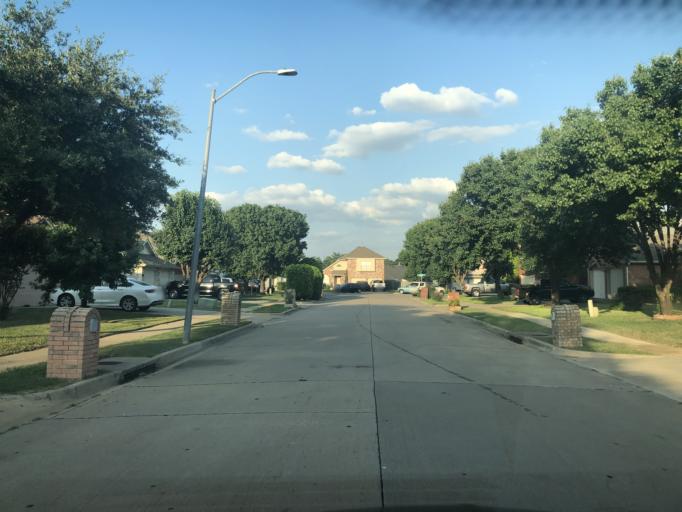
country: US
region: Texas
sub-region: Dallas County
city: Irving
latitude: 32.7936
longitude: -96.9621
